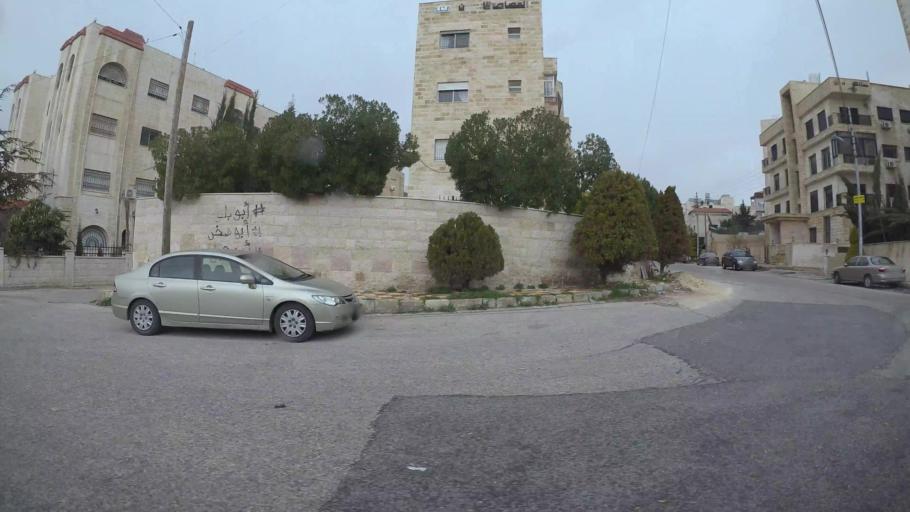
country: JO
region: Amman
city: Al Jubayhah
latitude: 31.9905
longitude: 35.8618
